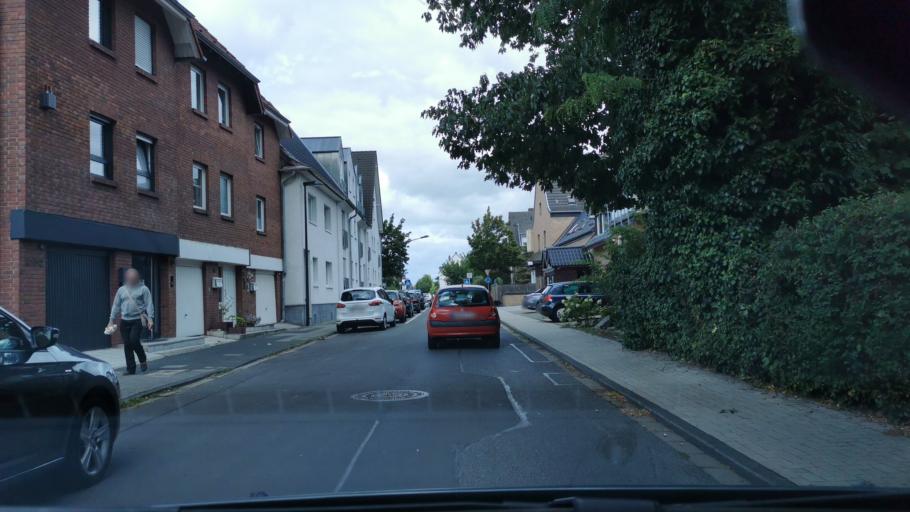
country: DE
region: North Rhine-Westphalia
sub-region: Regierungsbezirk Koln
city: Hurth
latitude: 50.8975
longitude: 6.8958
